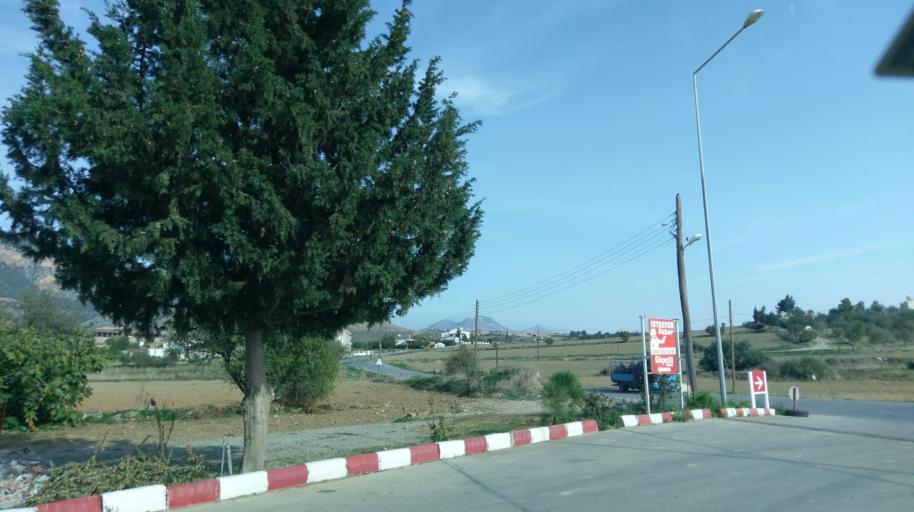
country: CY
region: Keryneia
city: Lapithos
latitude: 35.2828
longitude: 33.2129
